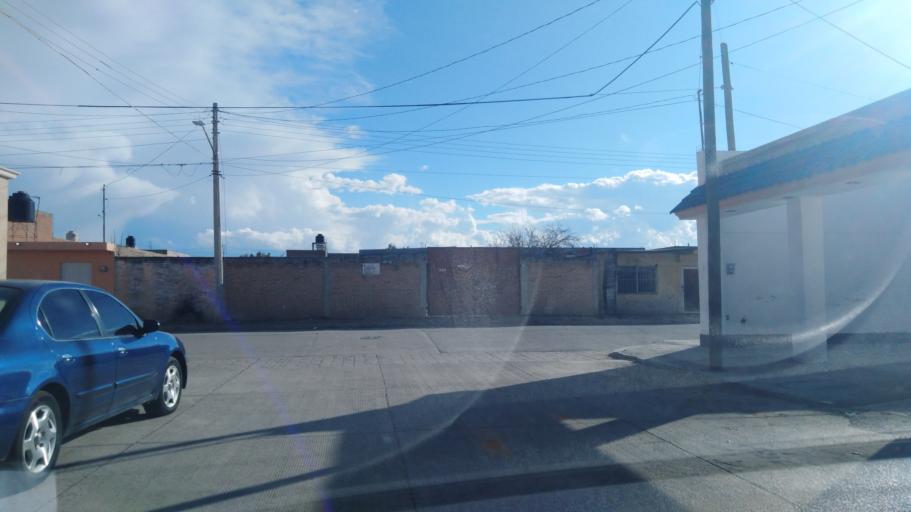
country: MX
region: Durango
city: Victoria de Durango
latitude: 24.0142
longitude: -104.6417
